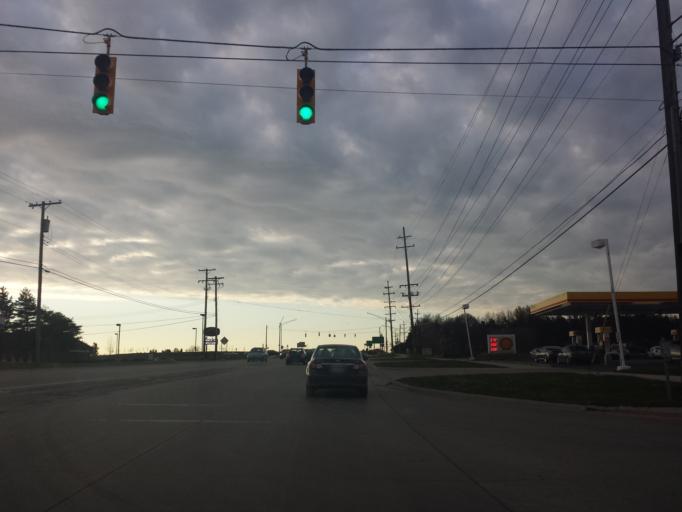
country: US
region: Michigan
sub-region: Oakland County
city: Rochester Hills
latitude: 42.6483
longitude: -83.1711
